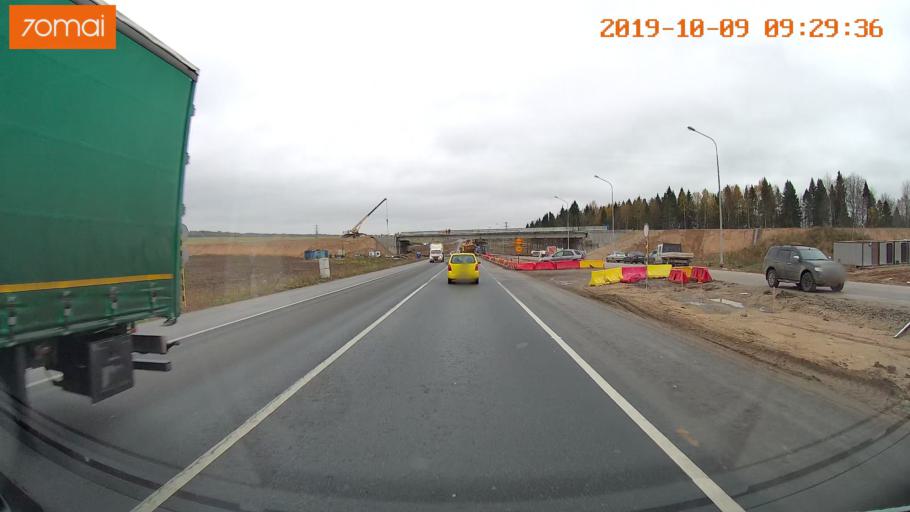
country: RU
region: Vologda
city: Vologda
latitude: 59.1331
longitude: 39.9565
